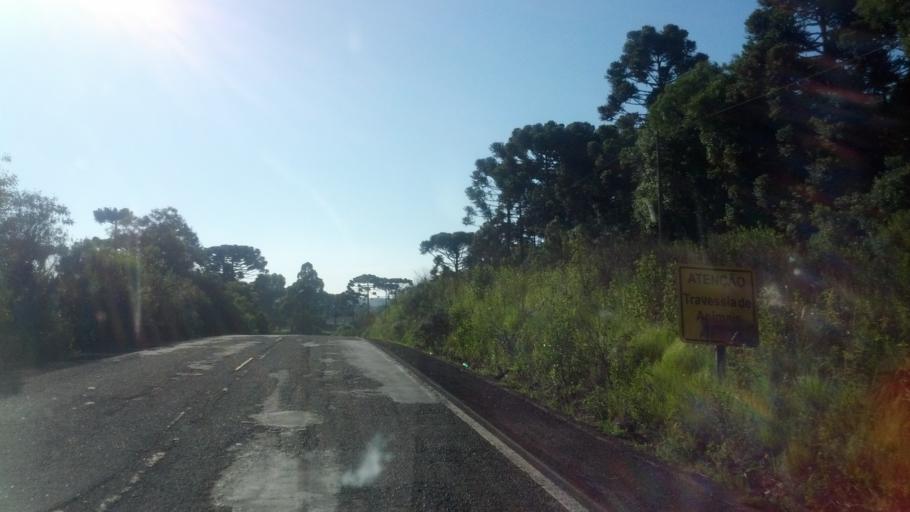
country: BR
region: Santa Catarina
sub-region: Lages
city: Lages
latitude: -27.9249
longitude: -50.5616
